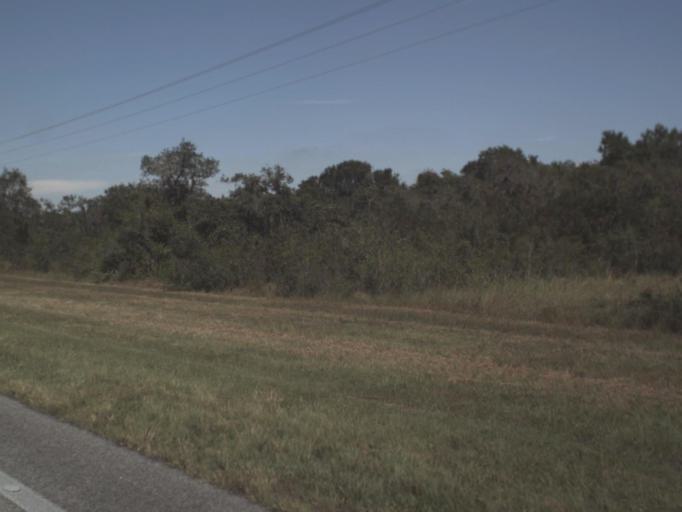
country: US
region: Florida
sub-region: Hendry County
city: Port LaBelle
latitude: 26.9416
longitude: -81.3164
